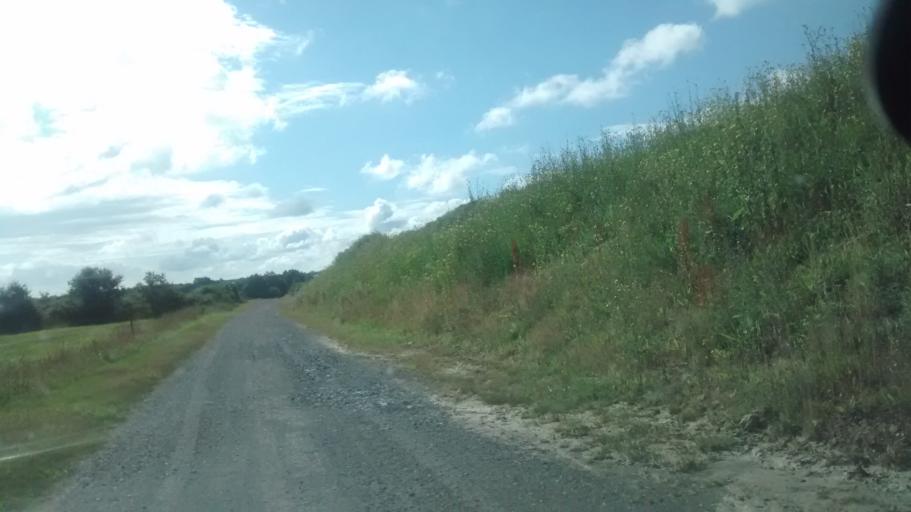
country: FR
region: Brittany
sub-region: Departement d'Ille-et-Vilaine
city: La Dominelais
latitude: 47.7784
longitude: -1.7235
